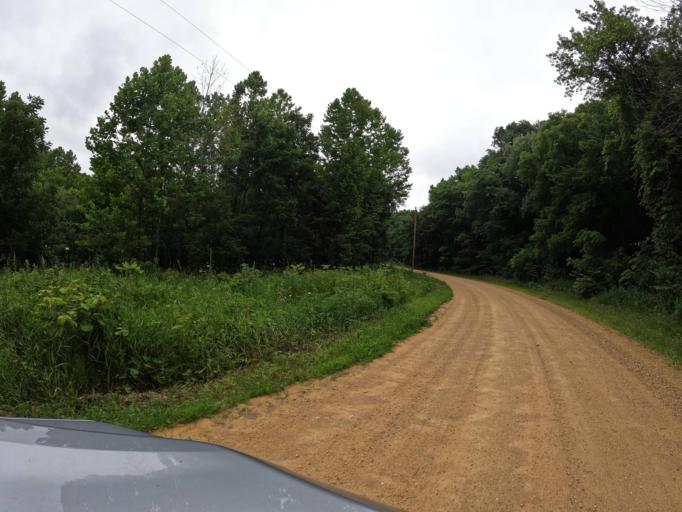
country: US
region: Illinois
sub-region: Carroll County
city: Savanna
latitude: 41.9967
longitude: -90.1771
